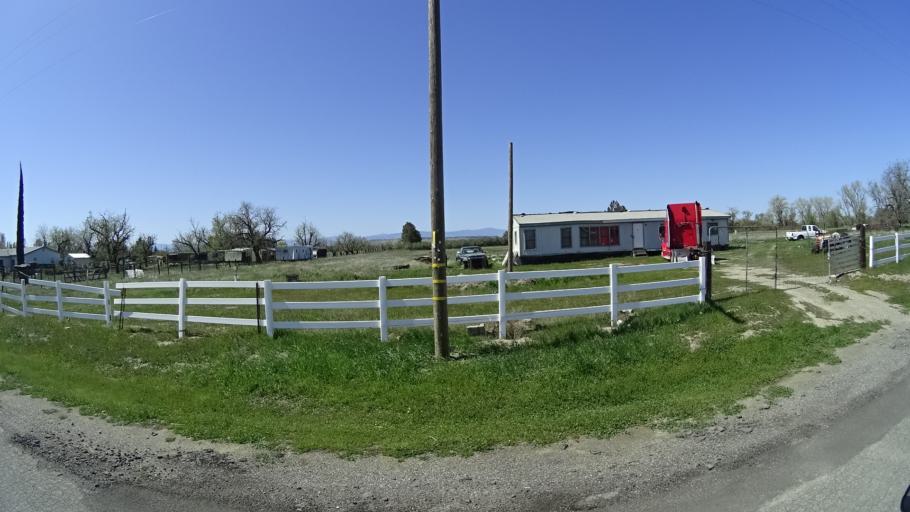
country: US
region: California
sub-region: Glenn County
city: Orland
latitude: 39.7825
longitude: -122.2476
